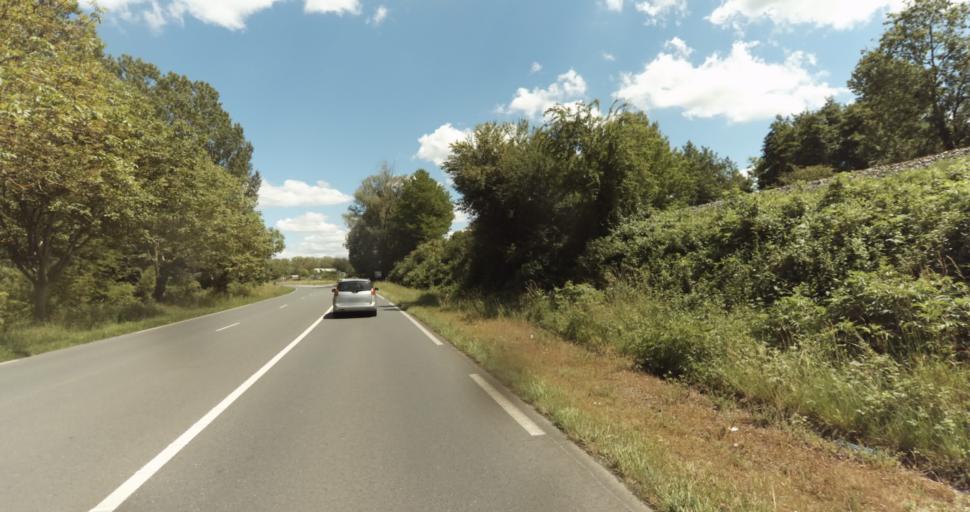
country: FR
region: Aquitaine
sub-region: Departement de la Dordogne
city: Belves
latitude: 44.8217
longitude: 0.9645
